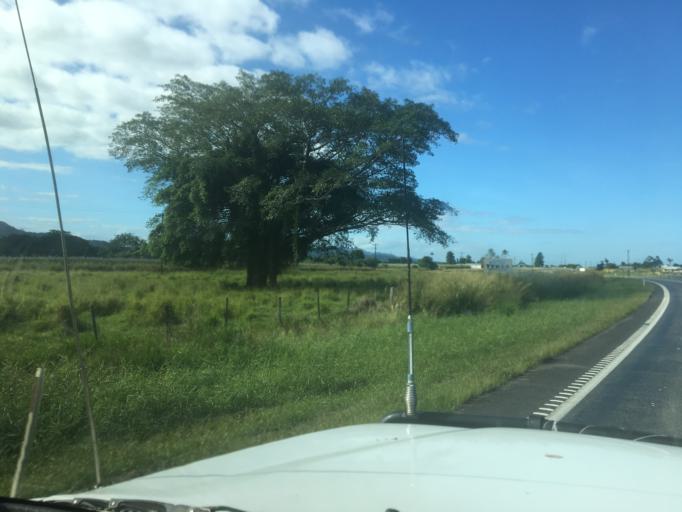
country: AU
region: Queensland
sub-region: Cassowary Coast
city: Innisfail
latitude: -17.3121
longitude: 145.9254
